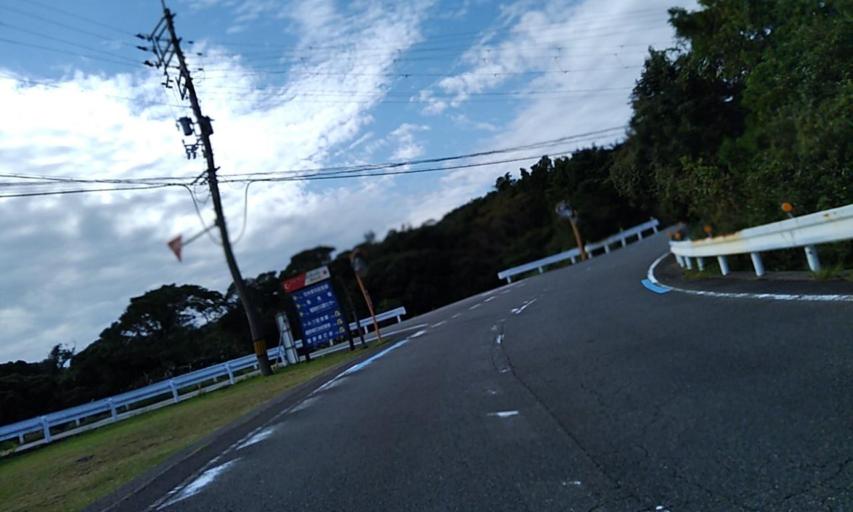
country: JP
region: Wakayama
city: Shingu
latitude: 33.4688
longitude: 135.8484
